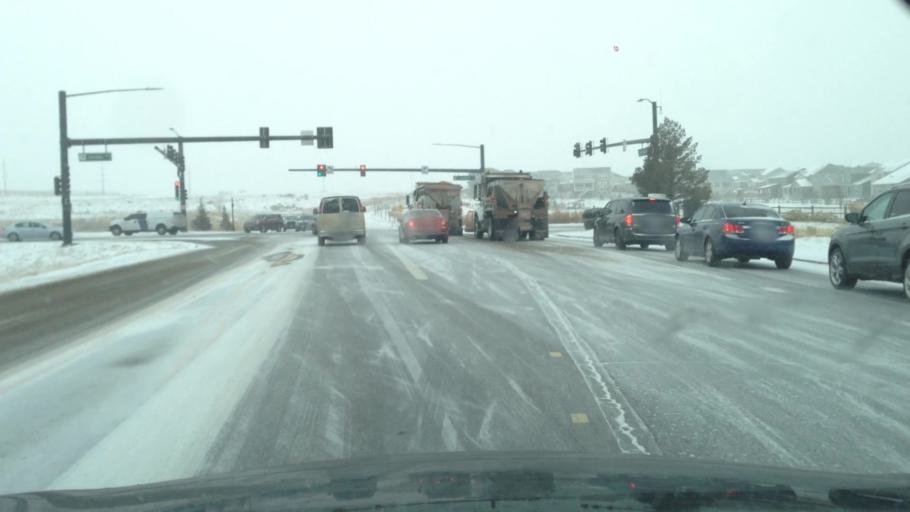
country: US
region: Colorado
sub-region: Douglas County
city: Stonegate
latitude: 39.5545
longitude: -104.7936
